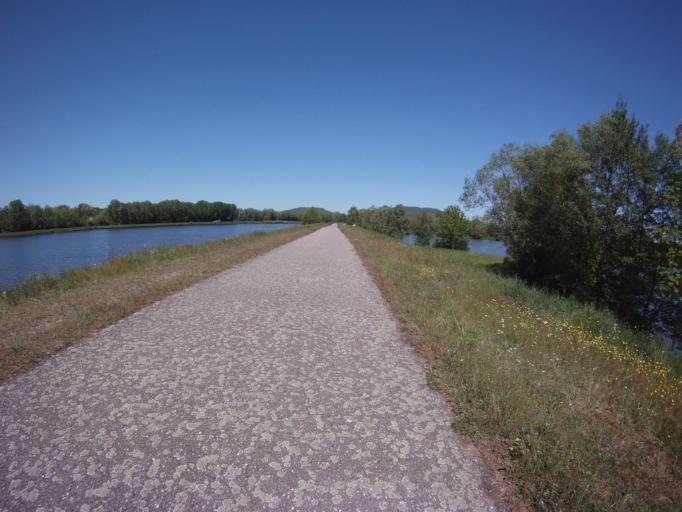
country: FR
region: Lorraine
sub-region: Departement de Meurthe-et-Moselle
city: Dommartin-les-Toul
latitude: 48.6614
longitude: 5.8949
